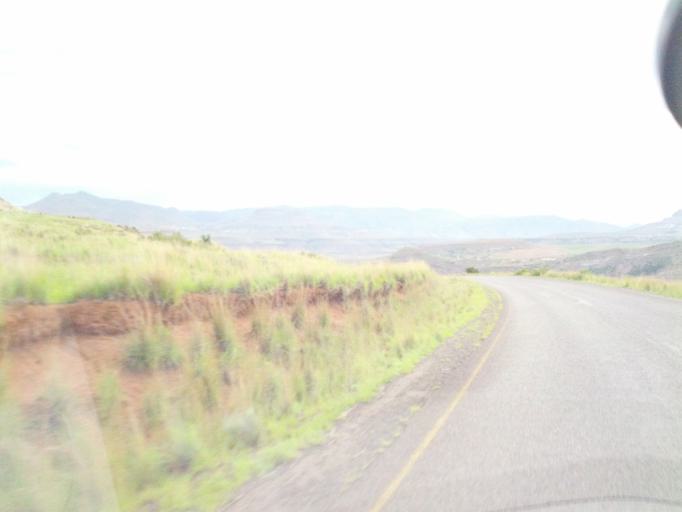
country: LS
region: Qacha's Nek
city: Qacha's Nek
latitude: -30.0507
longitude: 28.4935
